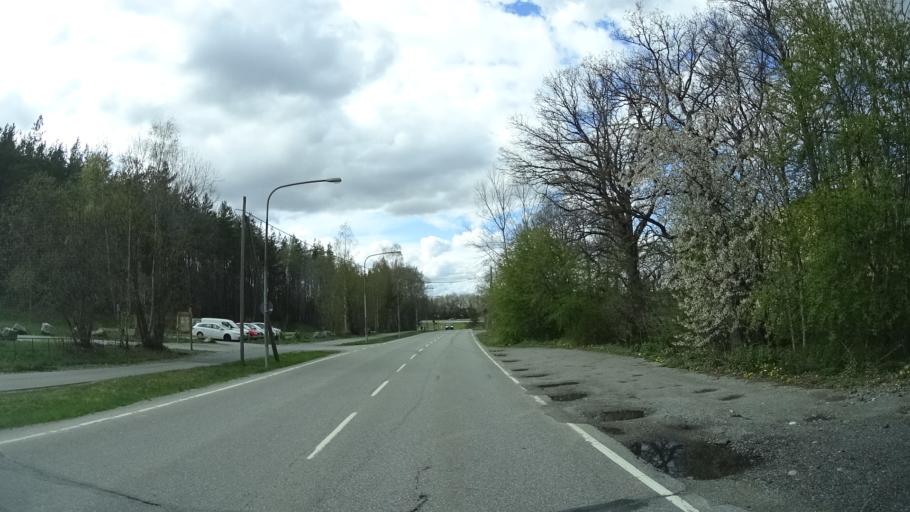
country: SE
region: Stockholm
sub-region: Nacka Kommun
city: Alta
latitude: 59.2629
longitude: 18.1476
